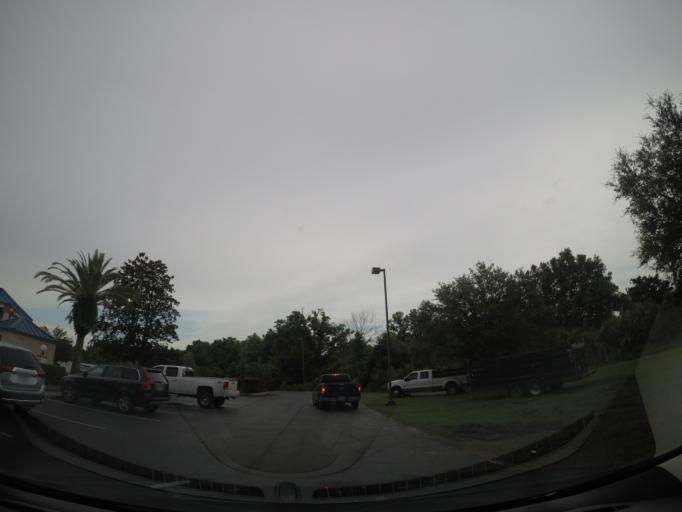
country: US
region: Florida
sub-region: Levy County
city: Chiefland
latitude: 29.4985
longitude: -82.8681
